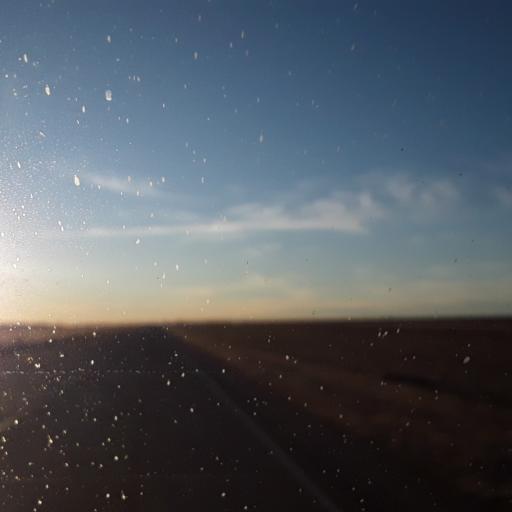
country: US
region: Colorado
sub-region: Cheyenne County
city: Cheyenne Wells
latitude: 38.8431
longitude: -102.2595
